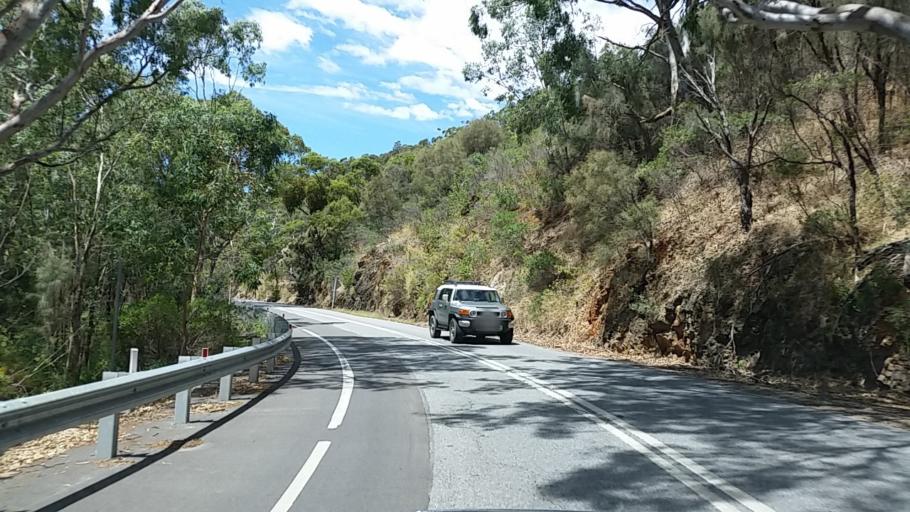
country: AU
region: South Australia
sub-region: Campbelltown
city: Athelstone
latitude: -34.8593
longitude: 138.7328
